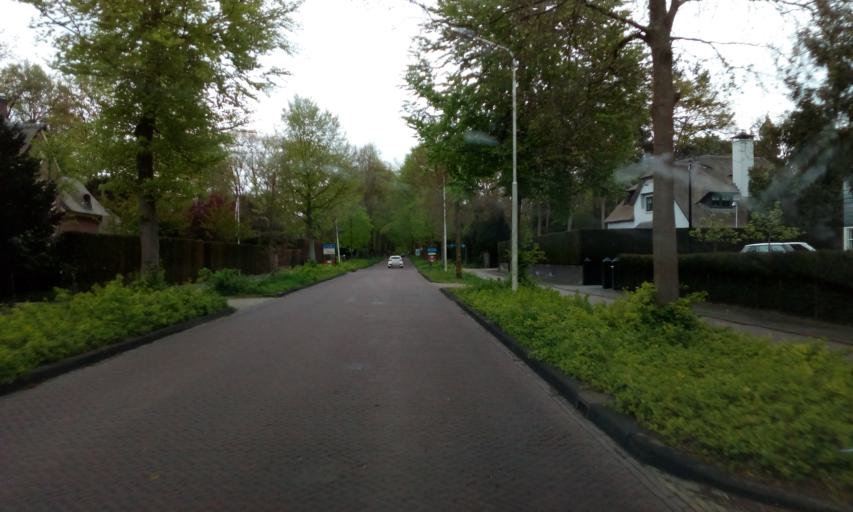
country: NL
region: North Holland
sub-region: Gemeente Laren
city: Laren
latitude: 52.2639
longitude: 5.2312
